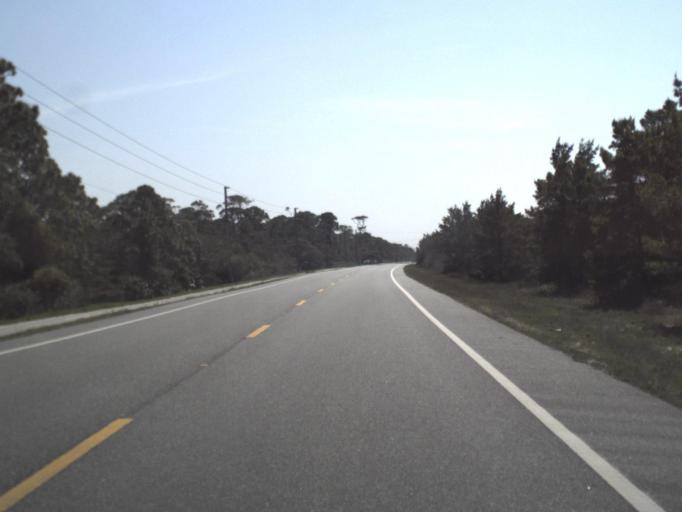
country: US
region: Florida
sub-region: Gulf County
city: Port Saint Joe
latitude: 29.7133
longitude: -85.3823
